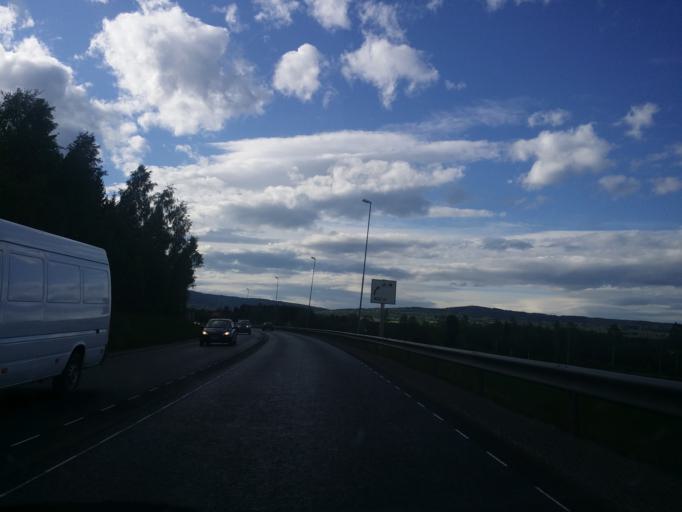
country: NO
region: Hedmark
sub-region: Hamar
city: Hamar
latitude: 60.8288
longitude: 11.0884
